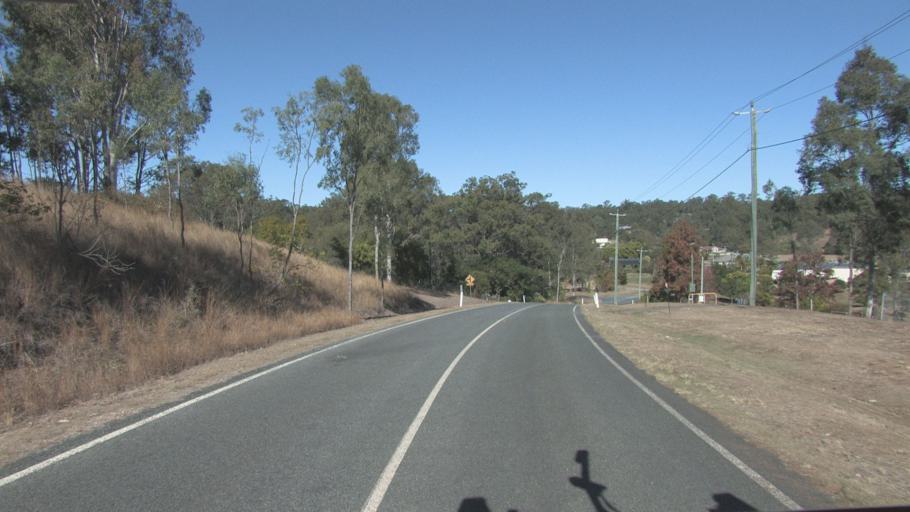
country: AU
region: Queensland
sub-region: Logan
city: Cedar Vale
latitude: -27.8874
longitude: 152.9951
